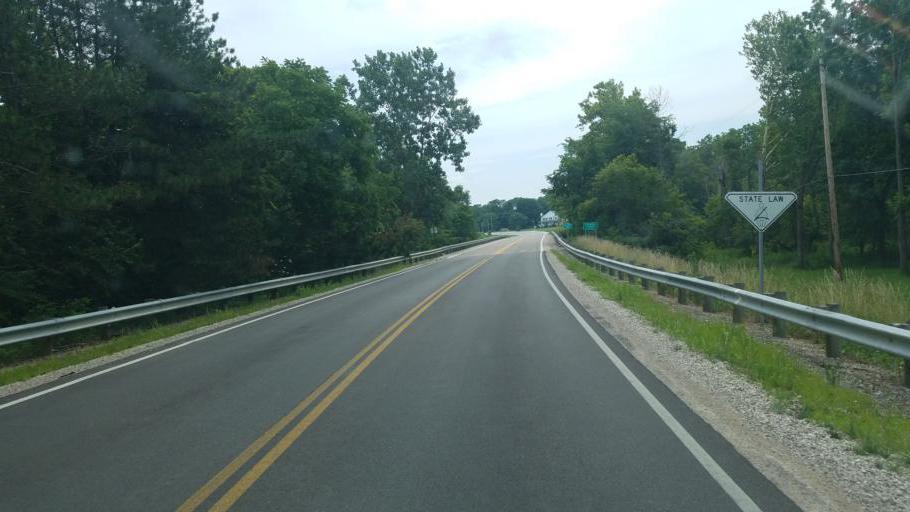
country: US
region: Ohio
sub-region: Madison County
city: Plain City
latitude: 40.0411
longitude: -83.2537
